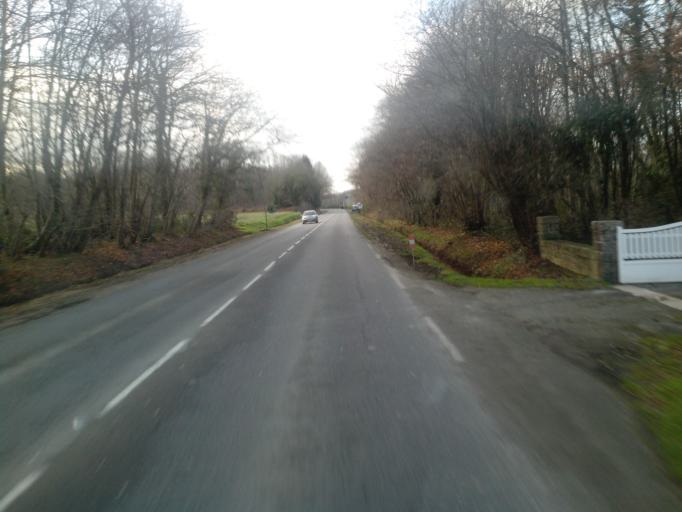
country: FR
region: Brittany
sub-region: Departement des Cotes-d'Armor
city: Plouer-sur-Rance
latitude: 48.5340
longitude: -2.0229
